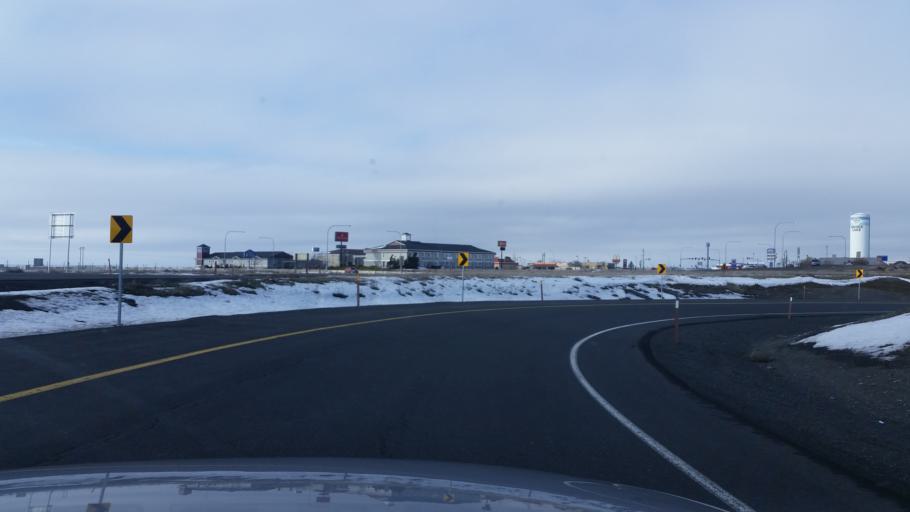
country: US
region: Washington
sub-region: Grant County
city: Moses Lake
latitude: 47.0978
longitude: -119.2444
